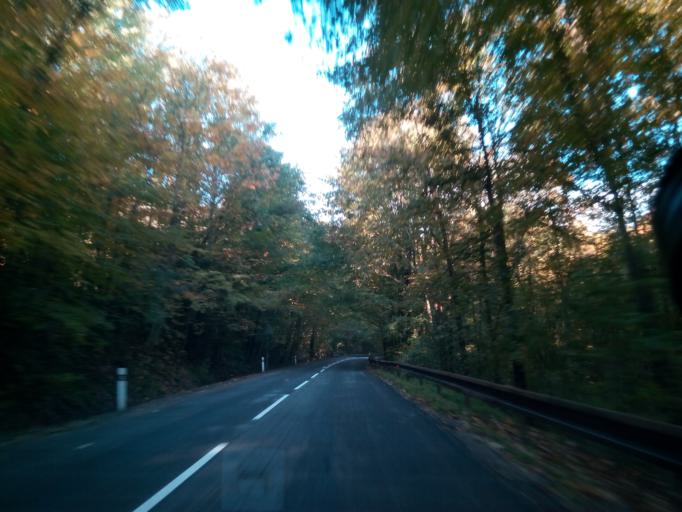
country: SK
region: Kosicky
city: Gelnica
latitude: 48.8329
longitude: 21.0566
